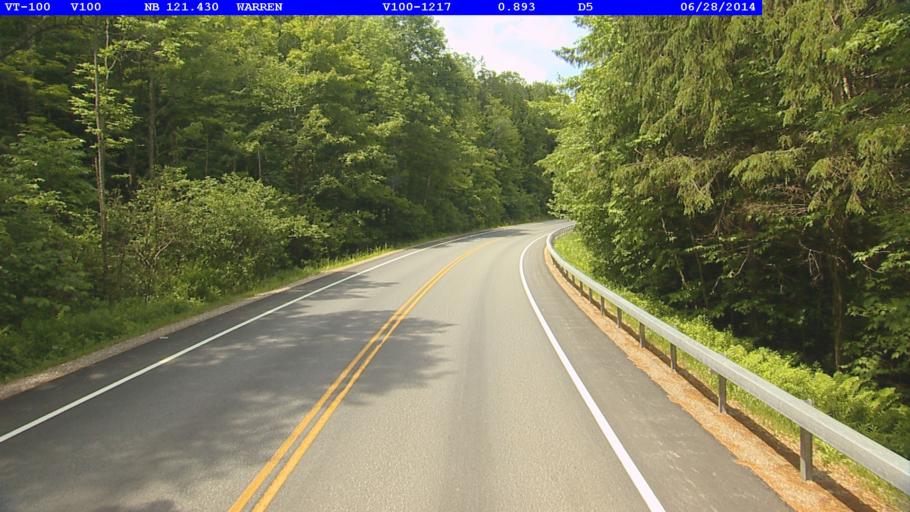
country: US
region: Vermont
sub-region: Washington County
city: Northfield
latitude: 44.0724
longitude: -72.8603
